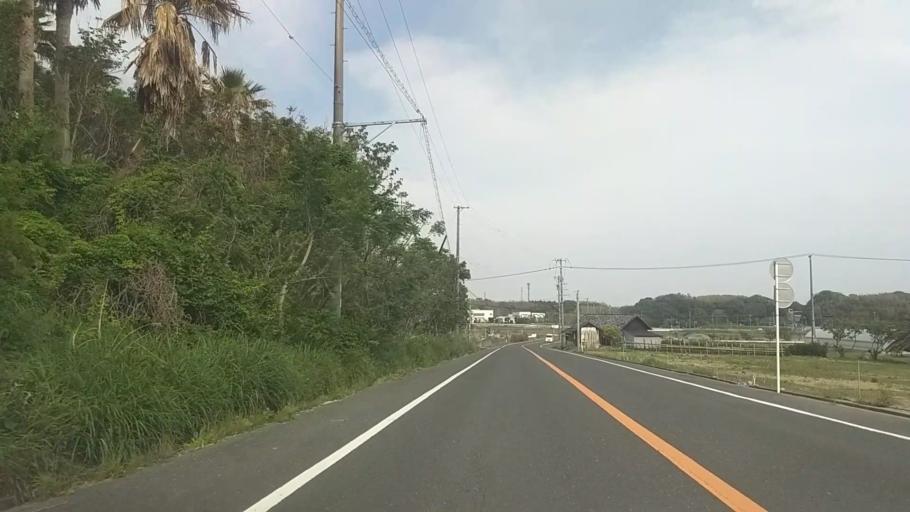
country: JP
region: Shizuoka
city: Kosai-shi
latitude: 34.7112
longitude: 137.6267
